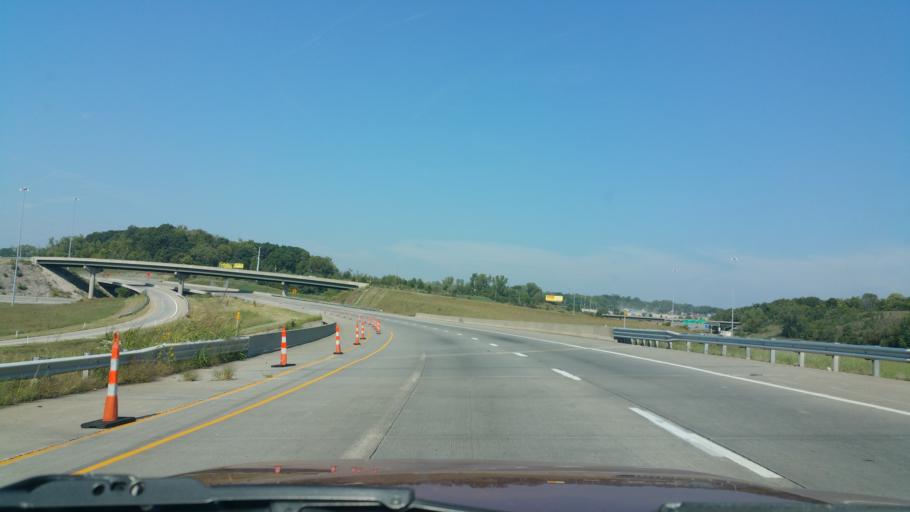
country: US
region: Kansas
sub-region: Wyandotte County
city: Kansas City
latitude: 39.1047
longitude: -94.6766
